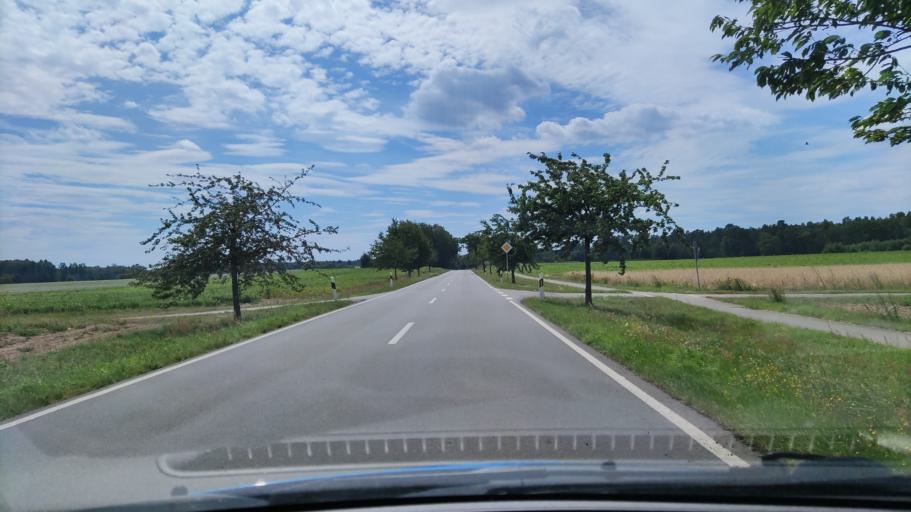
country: DE
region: Lower Saxony
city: Clenze
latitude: 52.9211
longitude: 10.9482
